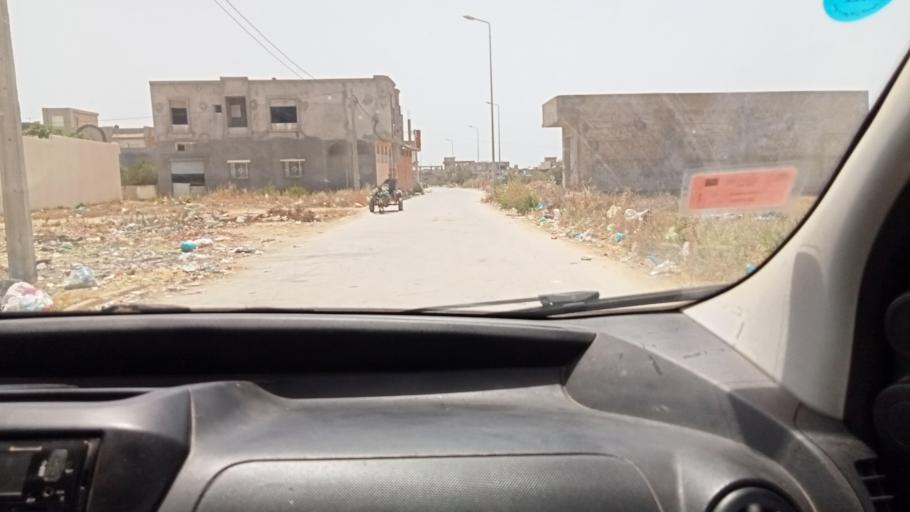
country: TN
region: Nabul
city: Qulaybiyah
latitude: 36.8596
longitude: 11.0849
